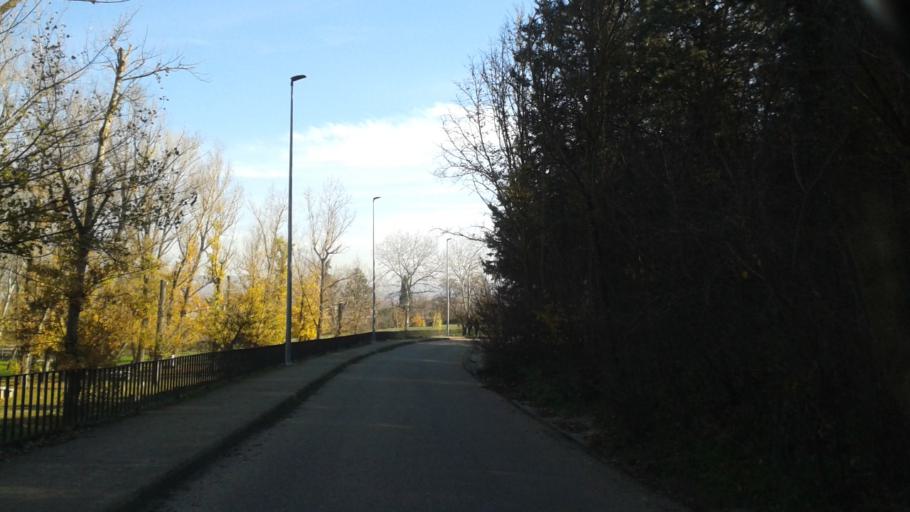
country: ES
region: Castille and Leon
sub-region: Provincia de Valladolid
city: Valladolid
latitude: 41.6693
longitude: -4.7412
